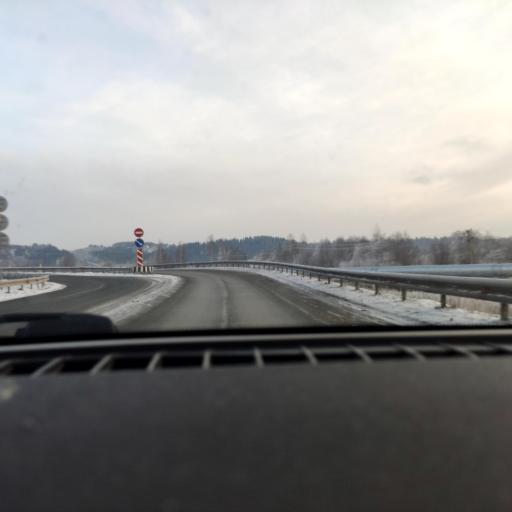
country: RU
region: Perm
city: Kondratovo
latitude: 57.9366
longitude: 56.1623
